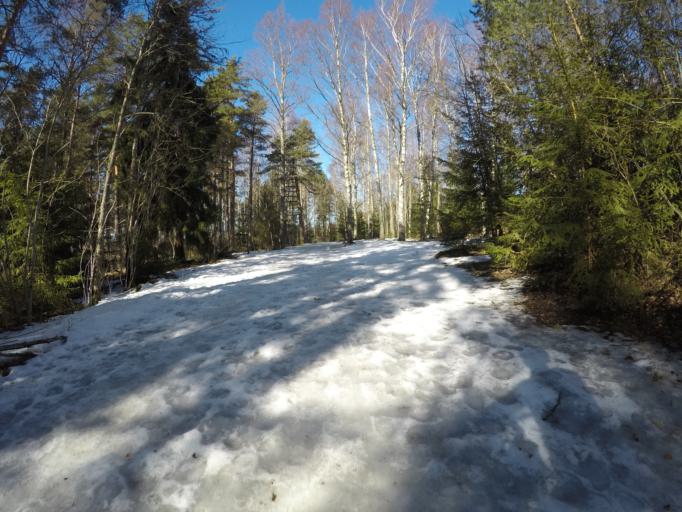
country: SE
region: Vaestmanland
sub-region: Vasteras
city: Vasteras
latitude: 59.5932
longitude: 16.6235
